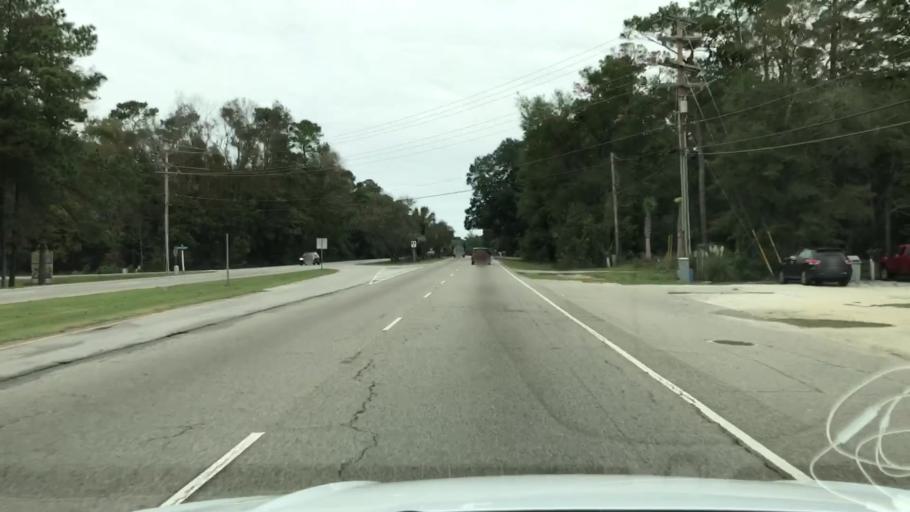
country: US
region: South Carolina
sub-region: Georgetown County
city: Murrells Inlet
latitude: 33.4746
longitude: -79.1029
